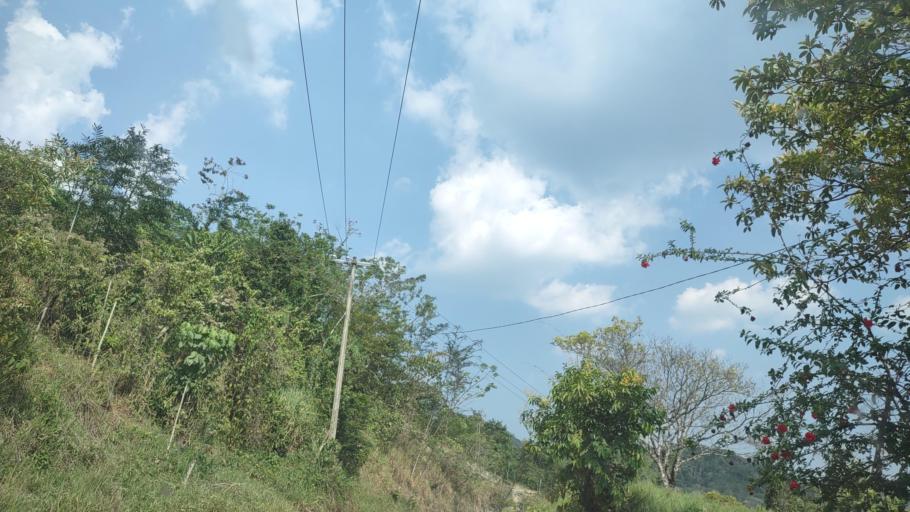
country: MX
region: Chiapas
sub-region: Tecpatan
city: Raudales Malpaso
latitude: 17.3271
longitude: -93.7462
